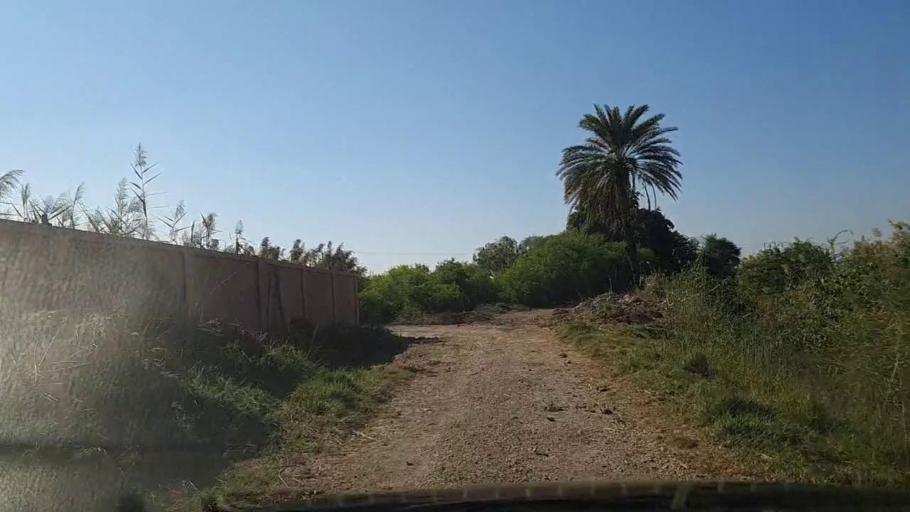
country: PK
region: Sindh
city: Thatta
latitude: 24.7014
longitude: 67.9040
